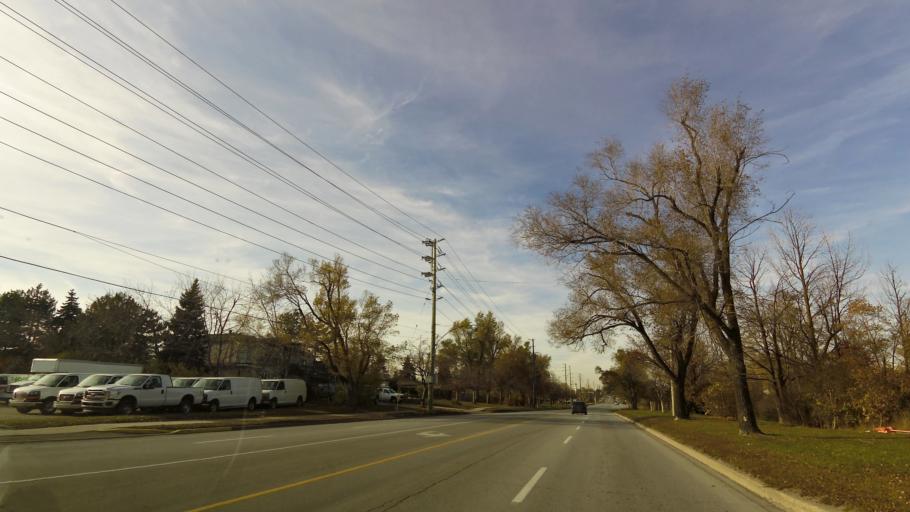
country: CA
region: Ontario
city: Brampton
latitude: 43.7180
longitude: -79.6849
